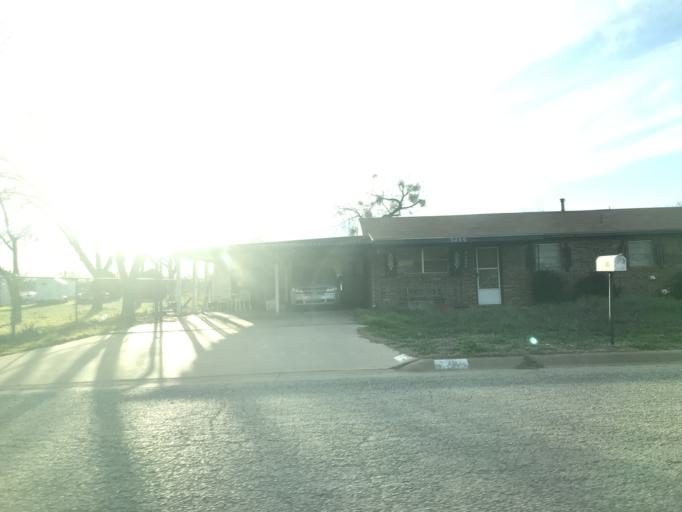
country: US
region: Texas
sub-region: Tom Green County
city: San Angelo
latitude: 31.4949
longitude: -100.4426
